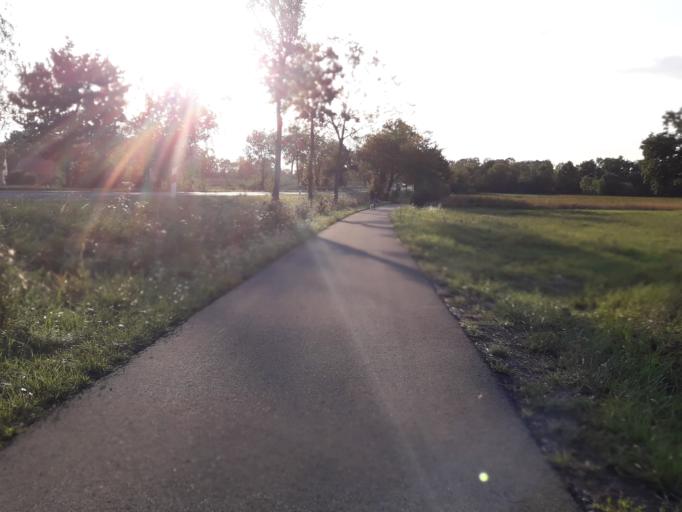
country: DE
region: North Rhine-Westphalia
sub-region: Regierungsbezirk Detmold
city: Salzkotten
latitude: 51.7122
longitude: 8.6525
